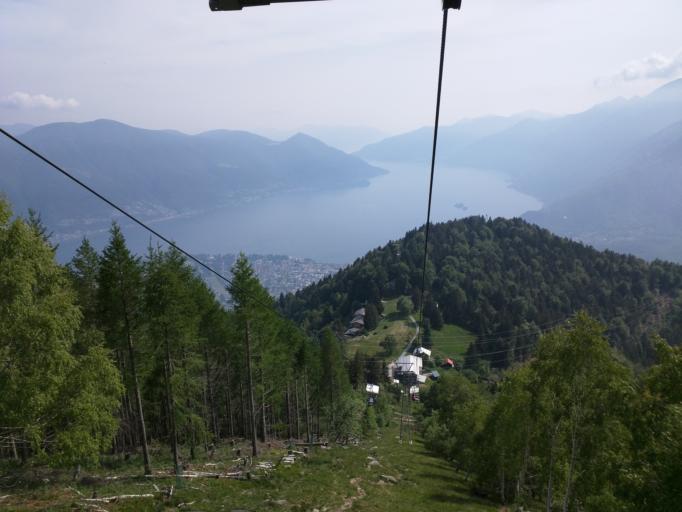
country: CH
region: Ticino
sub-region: Locarno District
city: Locarno
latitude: 46.1963
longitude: 8.7863
